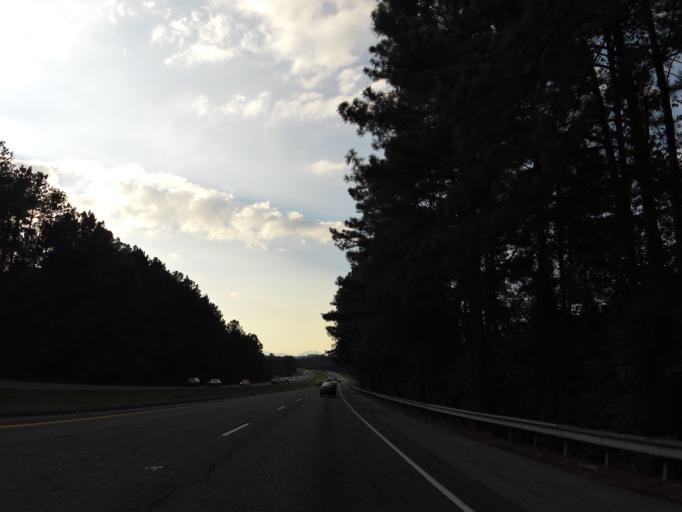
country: US
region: Tennessee
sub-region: Knox County
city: Farragut
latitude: 35.9446
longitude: -84.1546
